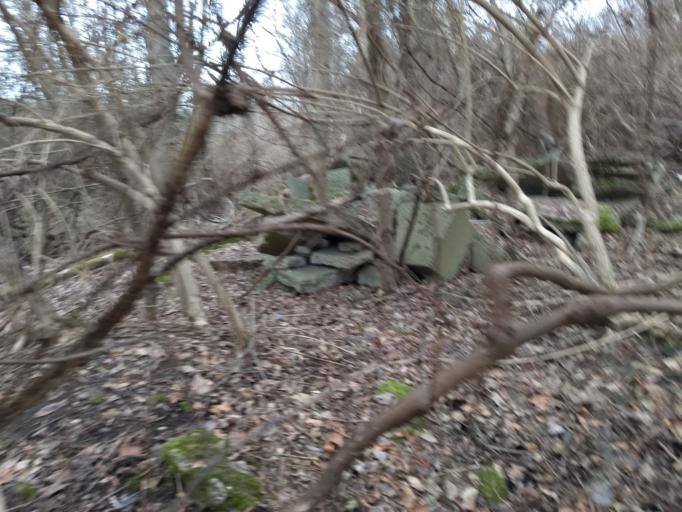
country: US
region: Pennsylvania
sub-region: Allegheny County
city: Homestead
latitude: 40.4089
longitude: -79.9357
